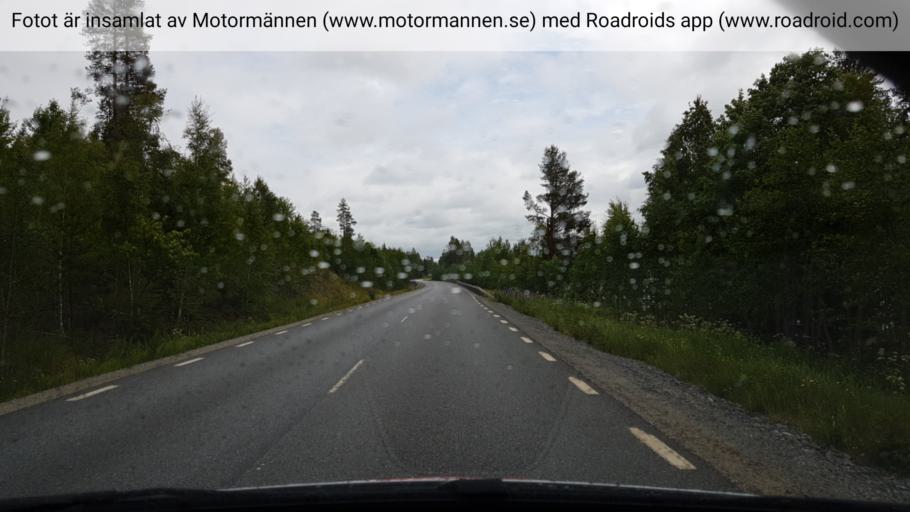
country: SE
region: Vaesterbotten
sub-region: Bjurholms Kommun
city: Bjurholm
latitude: 63.9500
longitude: 19.3291
